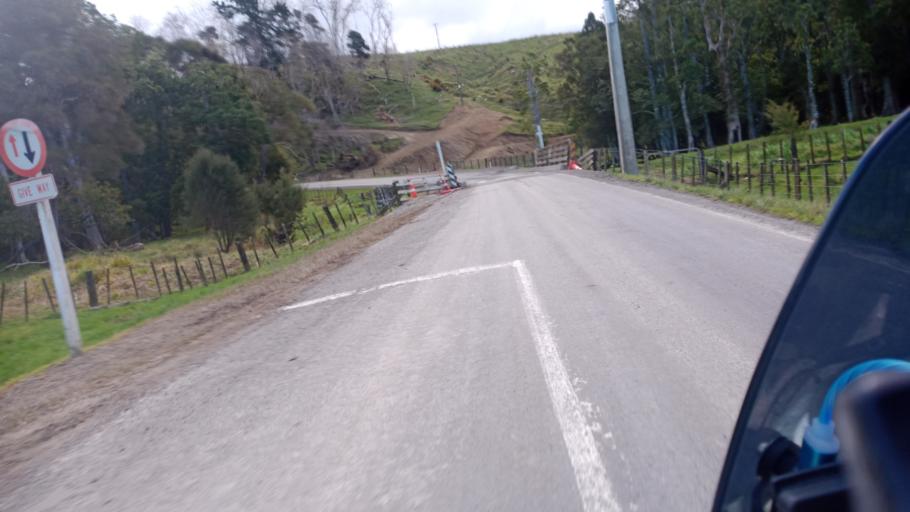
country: NZ
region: Gisborne
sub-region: Gisborne District
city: Gisborne
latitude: -38.3315
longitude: 178.2541
